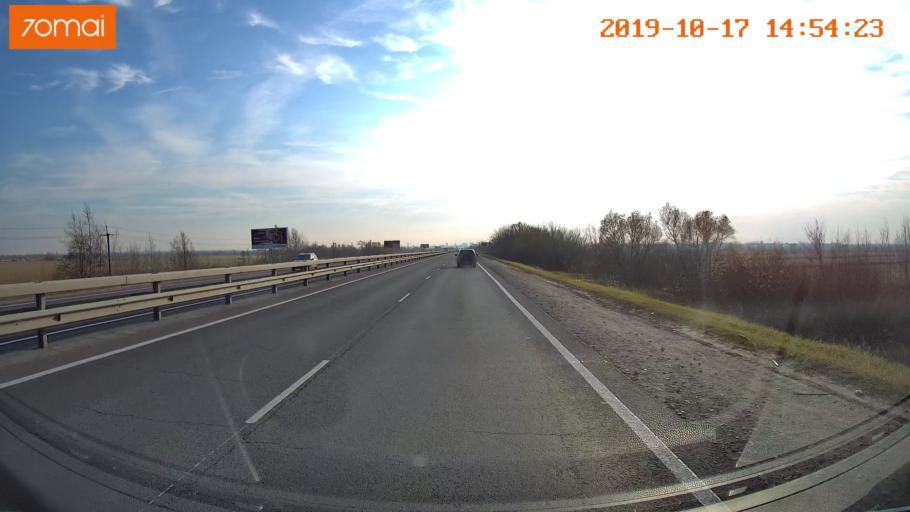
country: RU
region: Rjazan
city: Polyany
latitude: 54.6821
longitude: 39.8325
